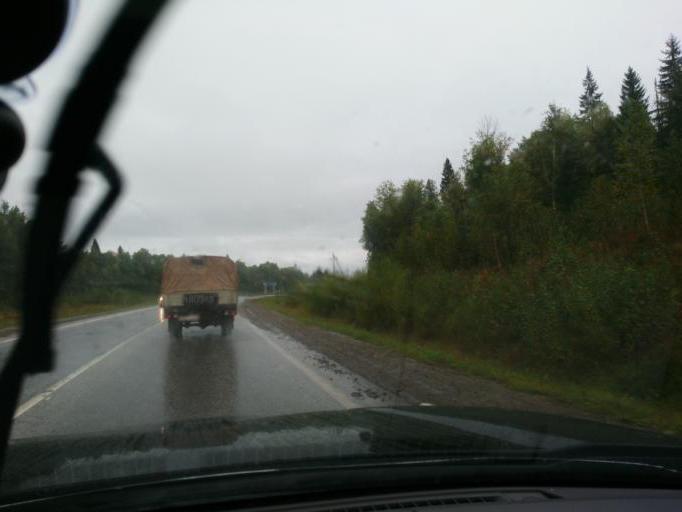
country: RU
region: Perm
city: Osa
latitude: 57.4297
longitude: 55.6224
